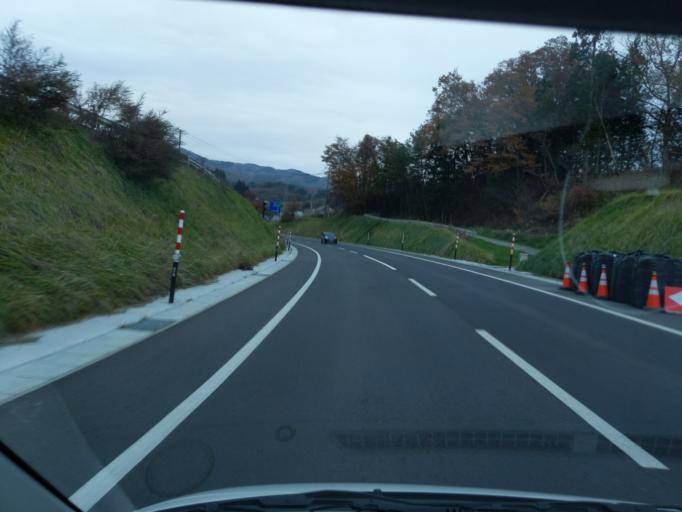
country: JP
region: Iwate
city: Kitakami
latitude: 39.2884
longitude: 141.2582
